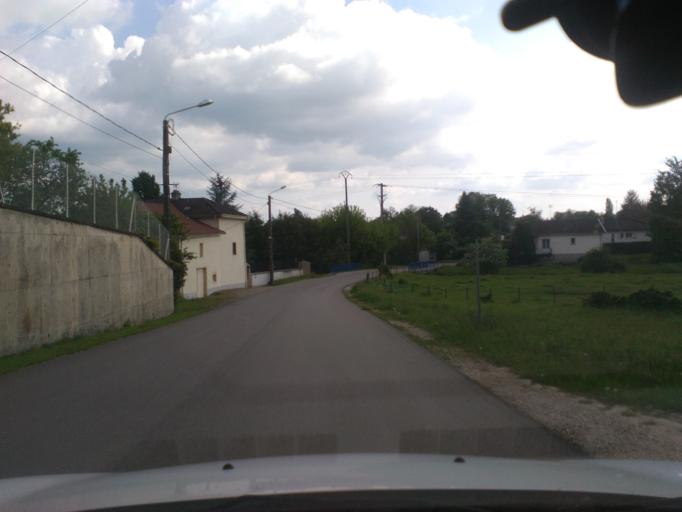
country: FR
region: Lorraine
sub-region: Departement des Vosges
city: Mirecourt
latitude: 48.3063
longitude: 6.1434
